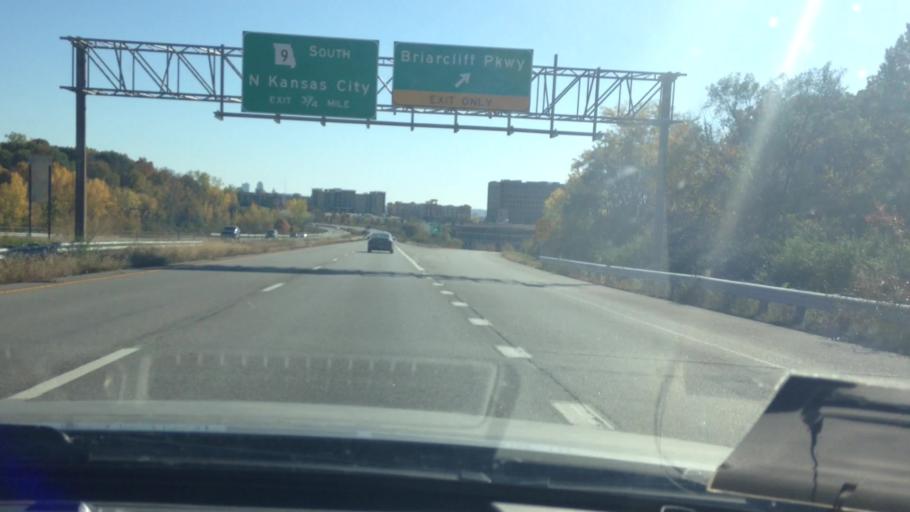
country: US
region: Missouri
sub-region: Platte County
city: Riverside
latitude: 39.1733
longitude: -94.5949
